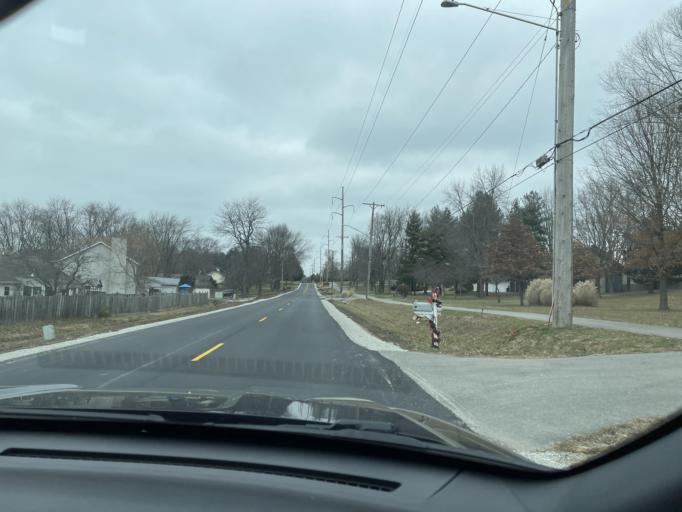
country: US
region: Illinois
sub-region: Sangamon County
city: Rochester
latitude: 39.7682
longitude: -89.5787
